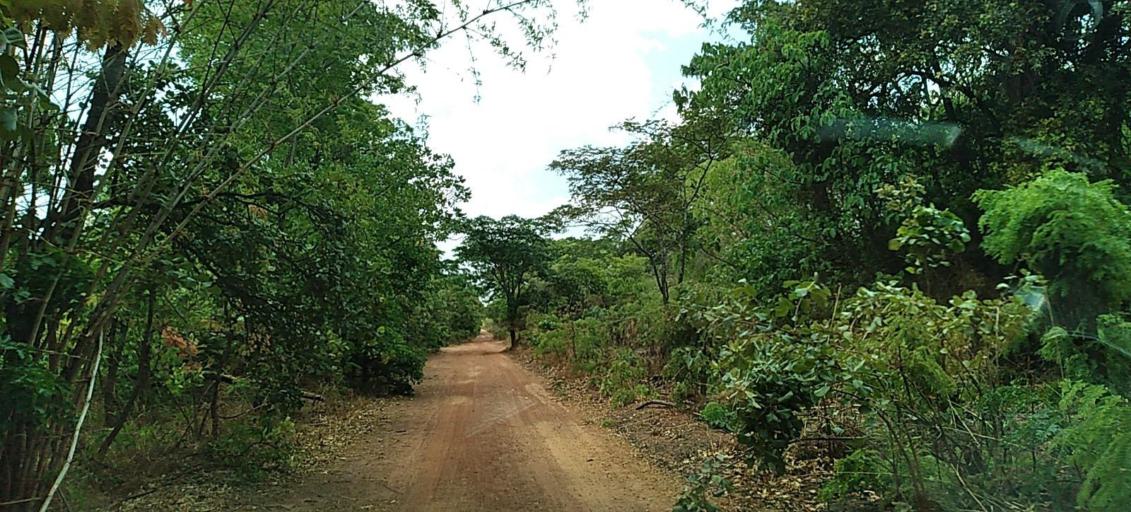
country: ZM
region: Copperbelt
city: Chingola
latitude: -12.5356
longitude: 27.6319
